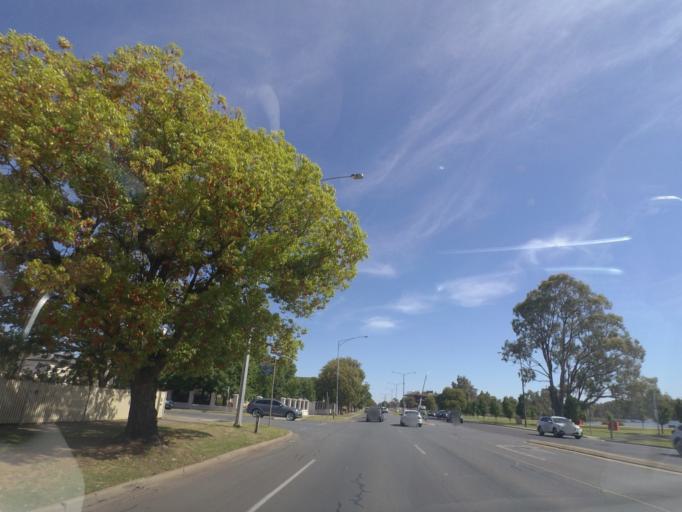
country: AU
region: Victoria
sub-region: Greater Shepparton
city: Shepparton
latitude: -36.3874
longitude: 145.3981
